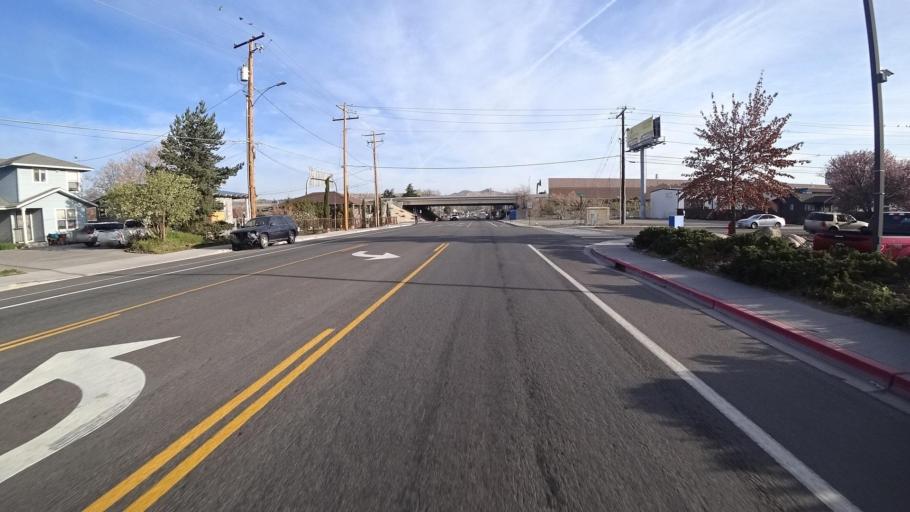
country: US
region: Nevada
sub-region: Washoe County
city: Reno
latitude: 39.5353
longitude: -119.7986
